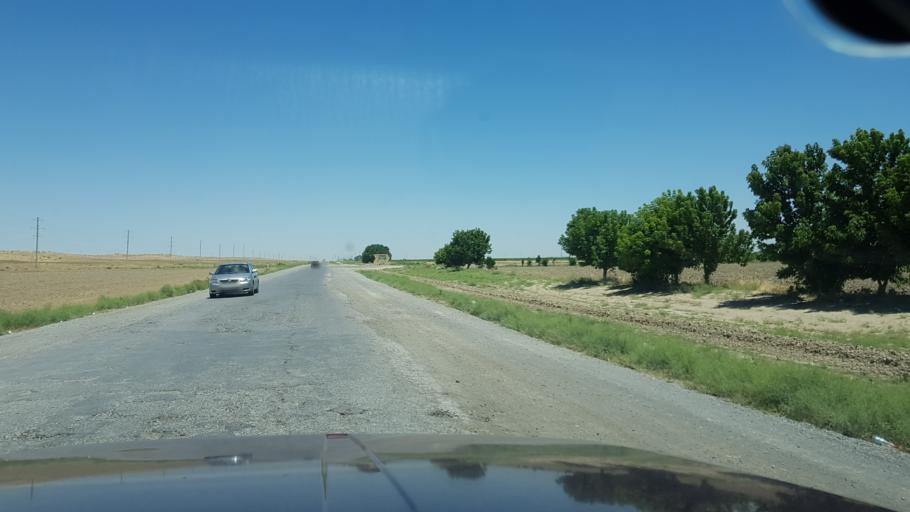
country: TM
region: Ahal
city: Annau
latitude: 37.8598
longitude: 58.7088
